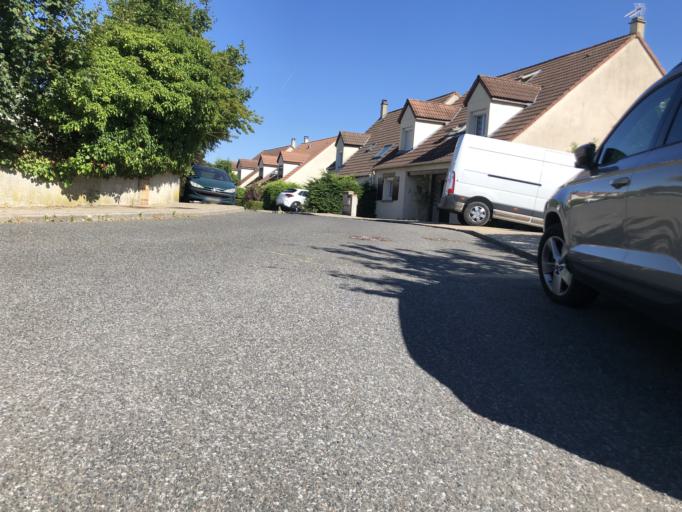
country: FR
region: Ile-de-France
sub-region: Departement des Yvelines
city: Triel-sur-Seine
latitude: 48.9787
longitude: 2.0181
